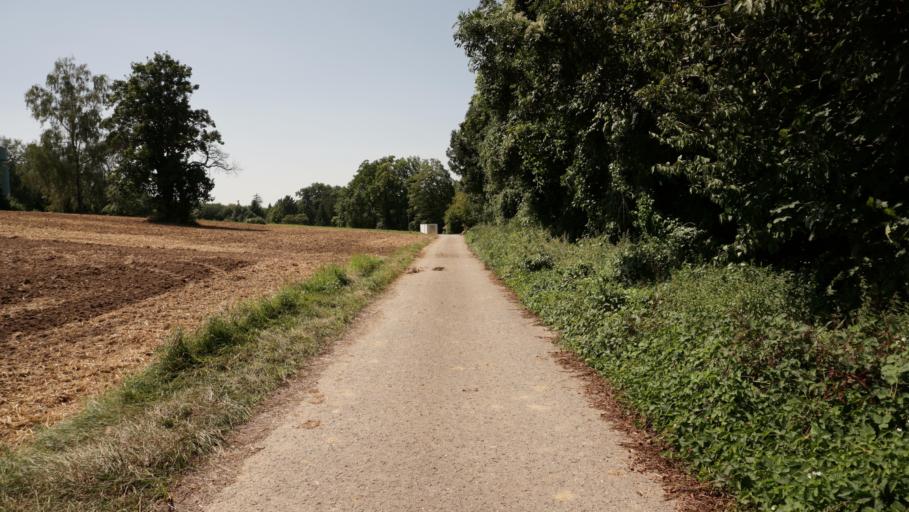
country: DE
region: Baden-Wuerttemberg
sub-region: Karlsruhe Region
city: Neckarzimmern
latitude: 49.3260
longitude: 9.1457
